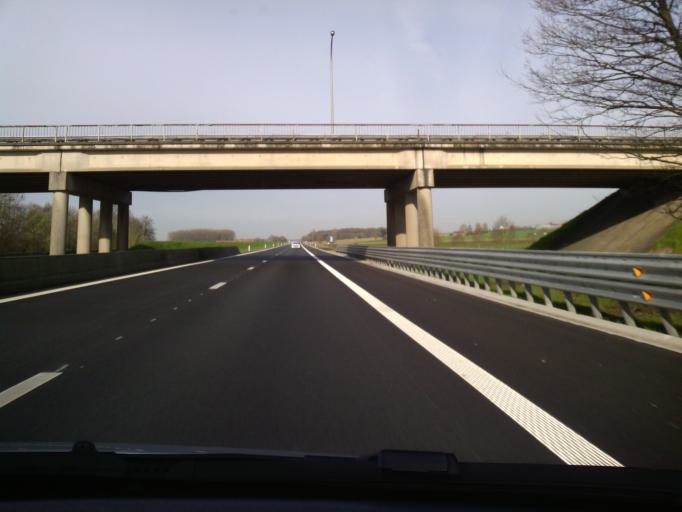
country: FR
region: Nord-Pas-de-Calais
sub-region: Departement du Nord
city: Bousbecque
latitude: 50.8219
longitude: 3.0710
